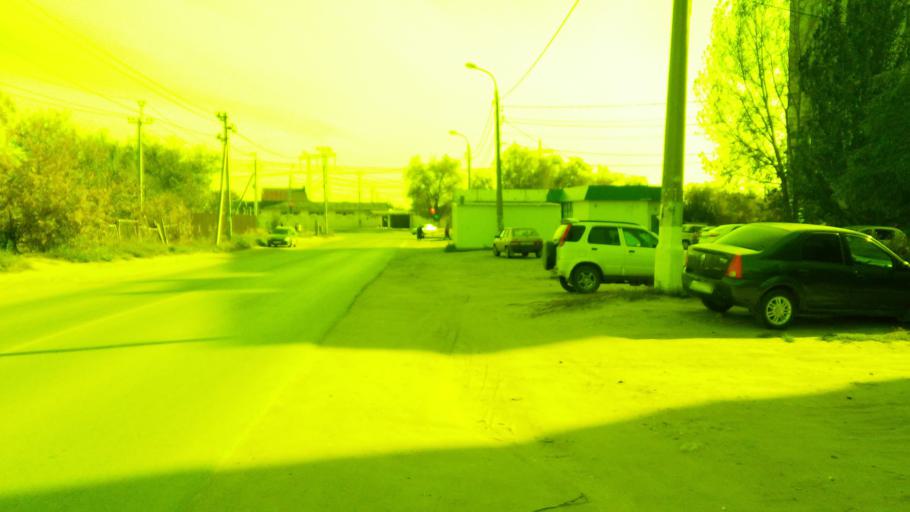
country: RU
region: Volgograd
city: Vodstroy
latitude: 48.8423
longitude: 44.6457
